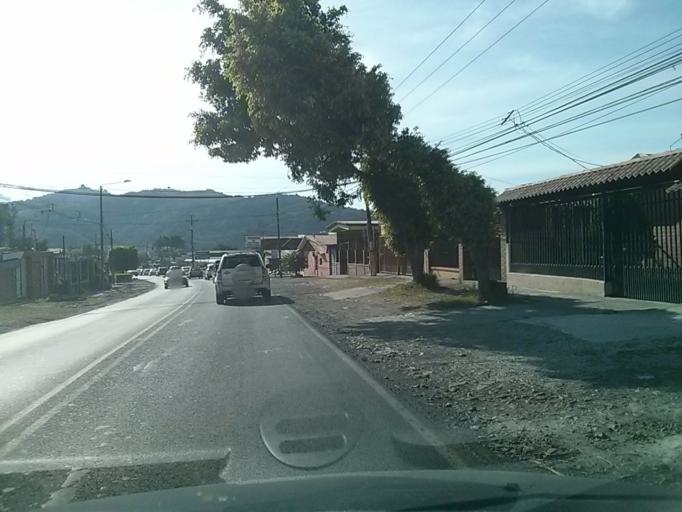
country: CR
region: Cartago
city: Cartago
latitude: 9.8804
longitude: -83.9331
